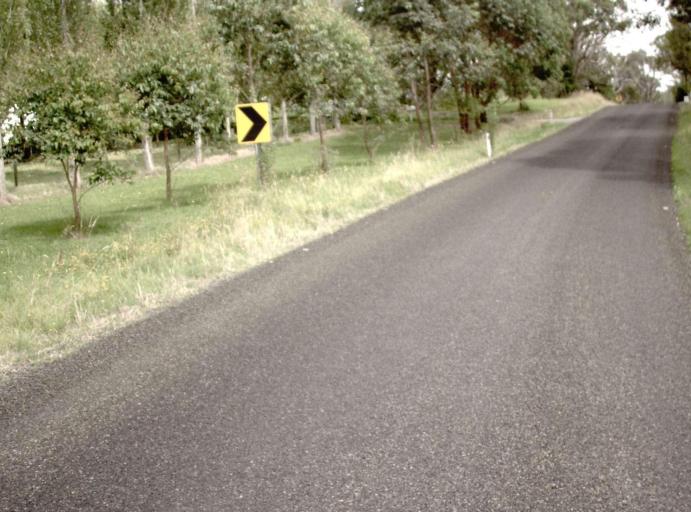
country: AU
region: Victoria
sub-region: Cardinia
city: Bunyip
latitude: -38.3369
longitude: 145.7027
